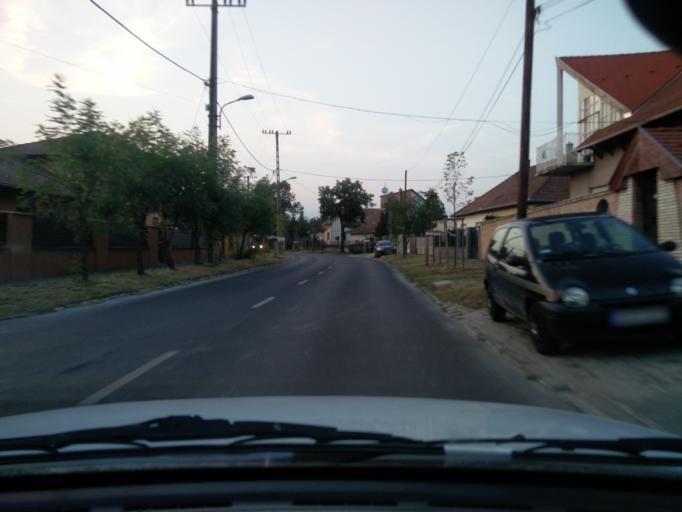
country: HU
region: Budapest
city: Budapest XXIII. keruelet
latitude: 47.3962
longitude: 19.0998
